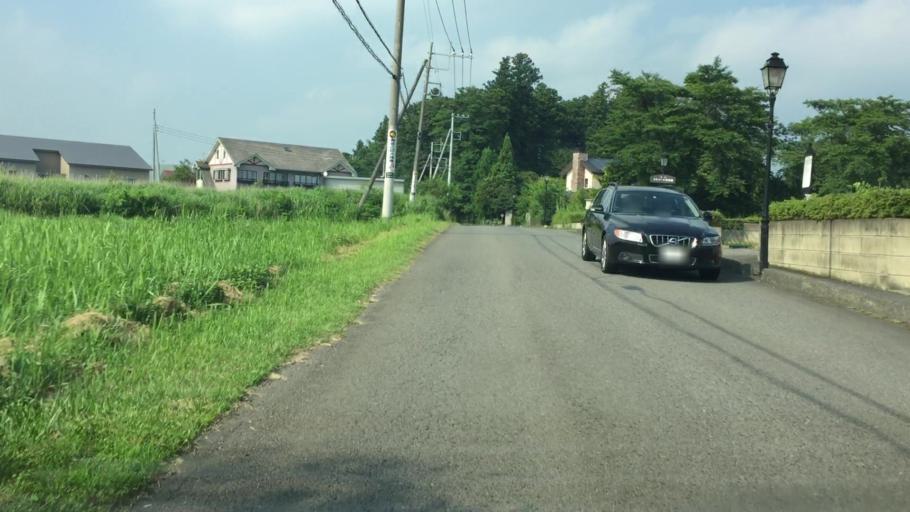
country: JP
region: Tochigi
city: Kuroiso
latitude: 37.0443
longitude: 140.0275
